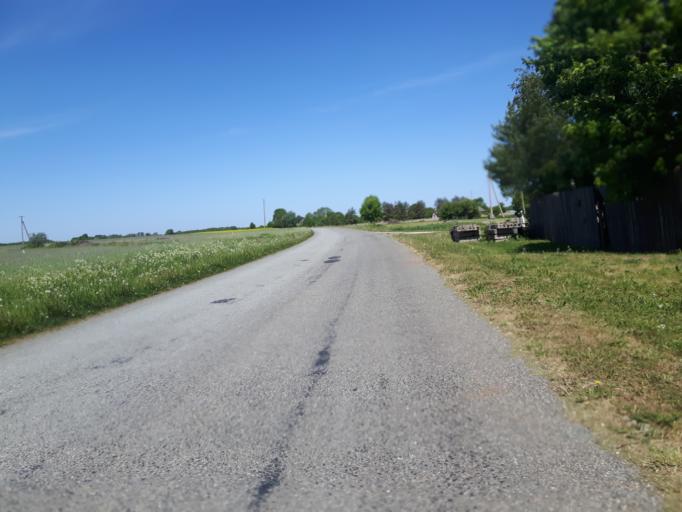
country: EE
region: Ida-Virumaa
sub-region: Aseri vald
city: Aseri
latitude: 59.4681
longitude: 26.8192
